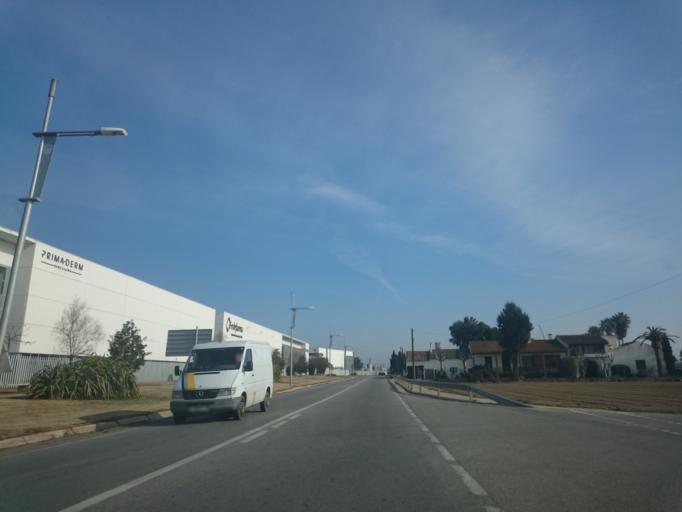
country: ES
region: Catalonia
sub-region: Provincia de Barcelona
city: Gava
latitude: 41.2919
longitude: 2.0156
